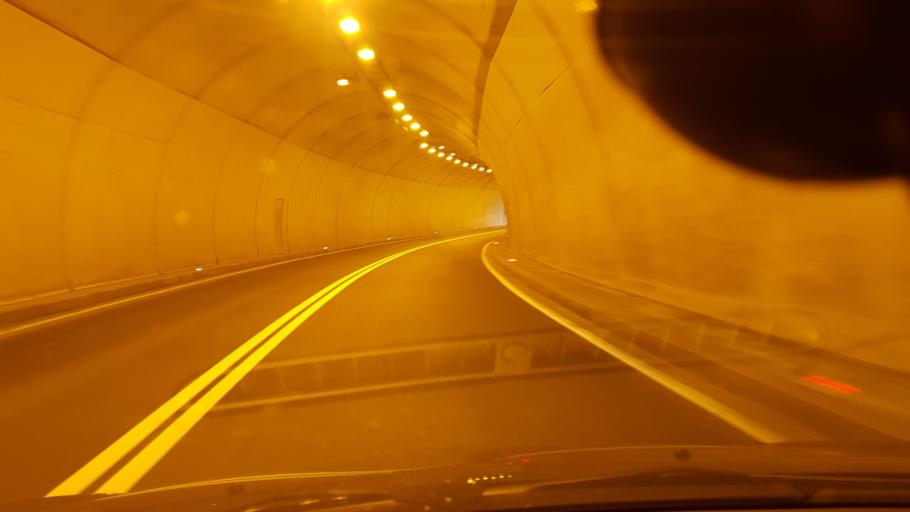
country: HR
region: Krapinsko-Zagorska
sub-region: Grad Krapina
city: Krapina
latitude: 46.2106
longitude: 15.8474
